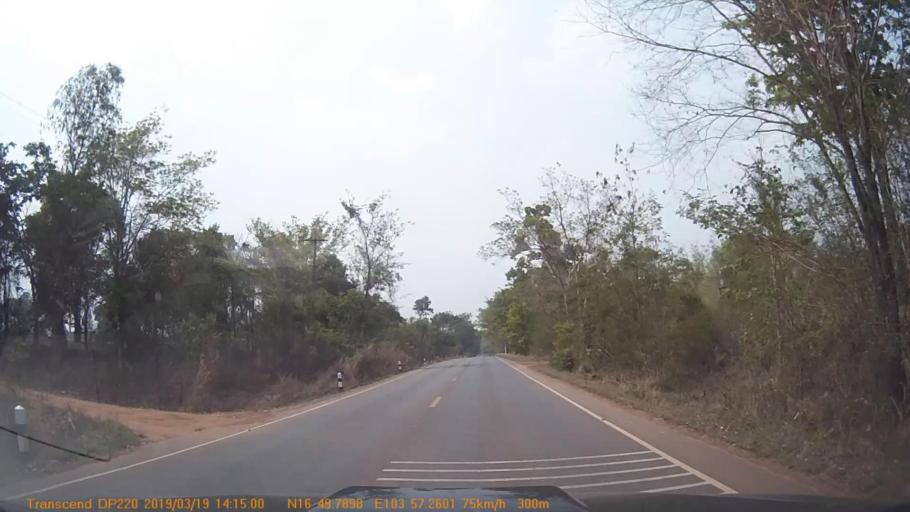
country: TH
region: Kalasin
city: Na Khu
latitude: 16.8303
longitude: 103.9540
